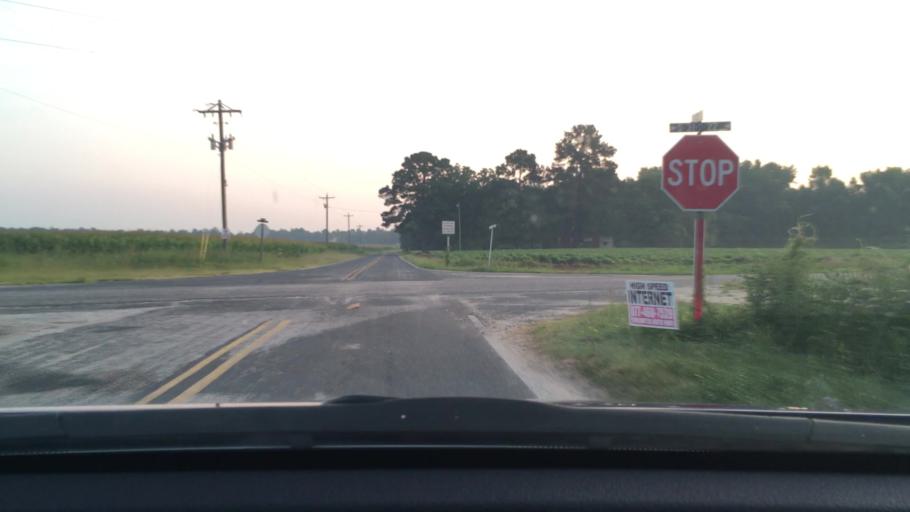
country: US
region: South Carolina
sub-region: Lee County
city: Bishopville
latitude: 34.1786
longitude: -80.1435
